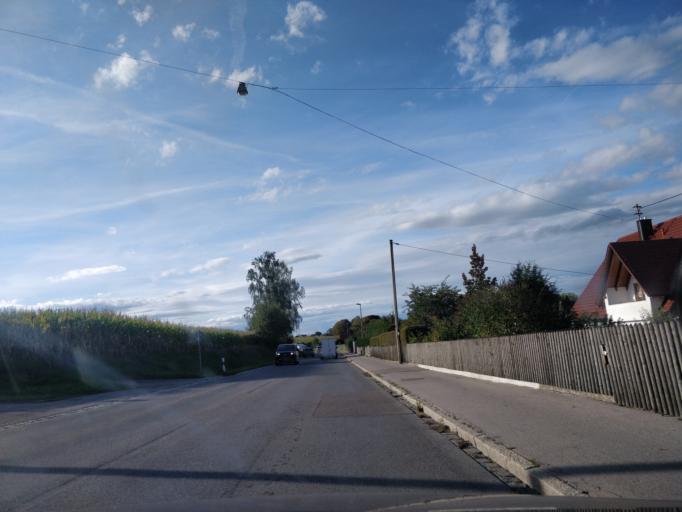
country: DE
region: Bavaria
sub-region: Swabia
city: Friedberg
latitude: 48.3398
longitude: 11.0003
